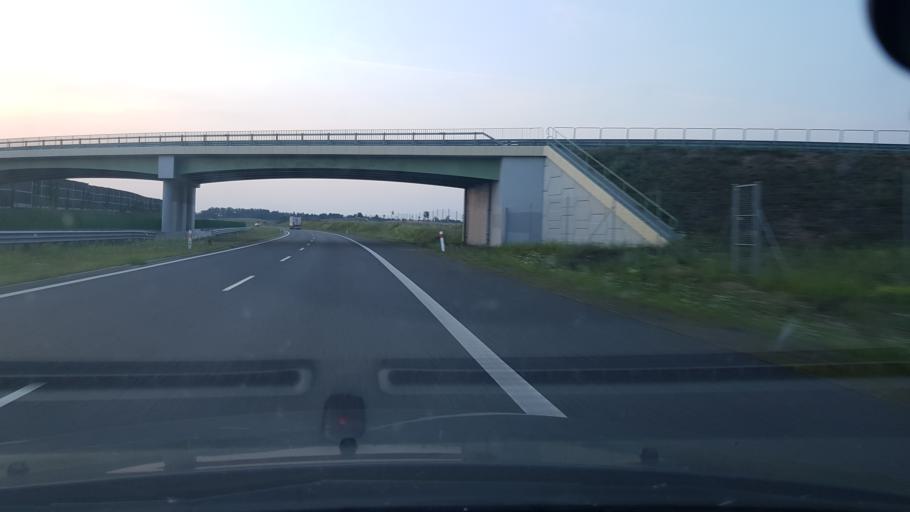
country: PL
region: Warmian-Masurian Voivodeship
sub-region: Powiat nidzicki
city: Nidzica
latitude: 53.4367
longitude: 20.3403
